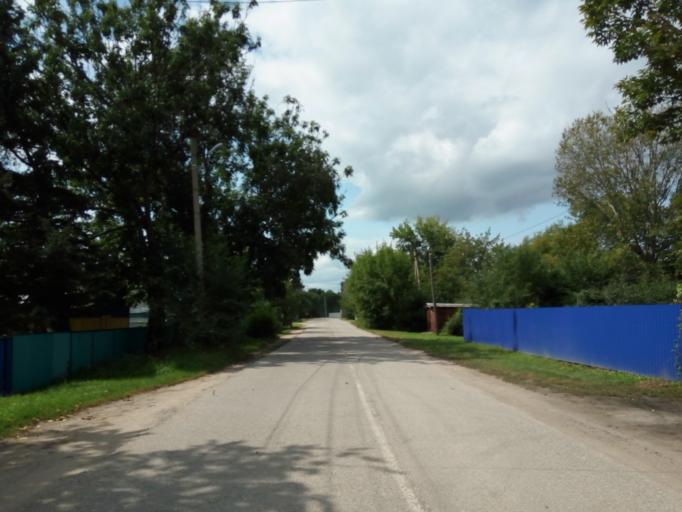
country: RU
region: Primorskiy
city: Dal'nerechensk
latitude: 45.9482
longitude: 133.8215
